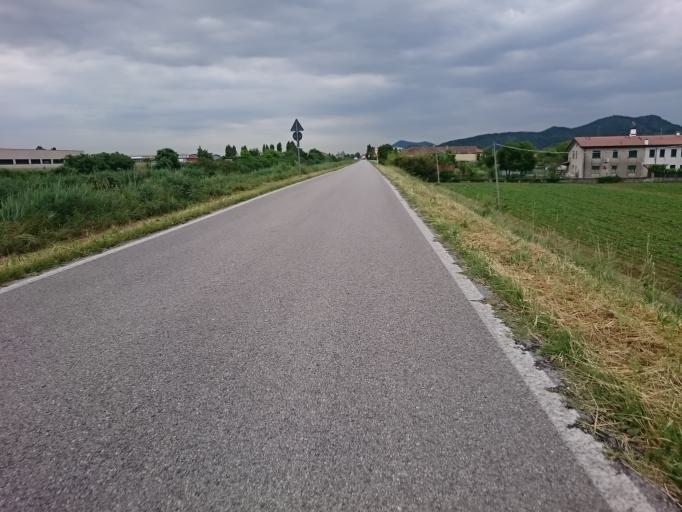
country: IT
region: Veneto
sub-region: Provincia di Padova
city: Terradura
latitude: 45.3280
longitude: 11.8147
